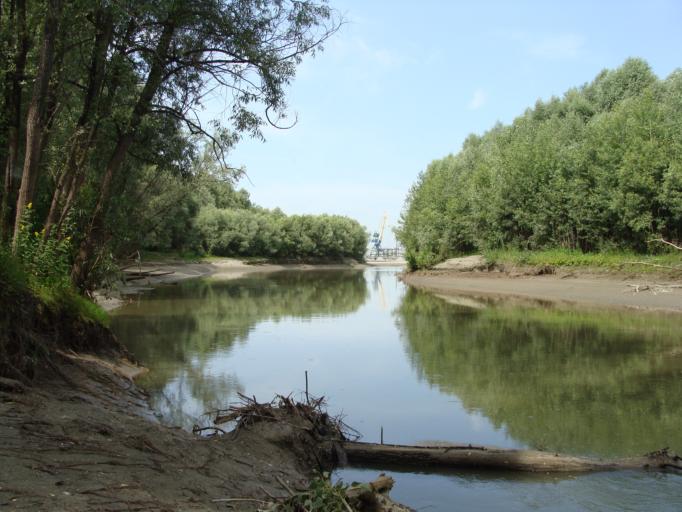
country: RU
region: Altai Krai
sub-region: Gorod Barnaulskiy
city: Barnaul
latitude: 53.3823
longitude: 83.8258
